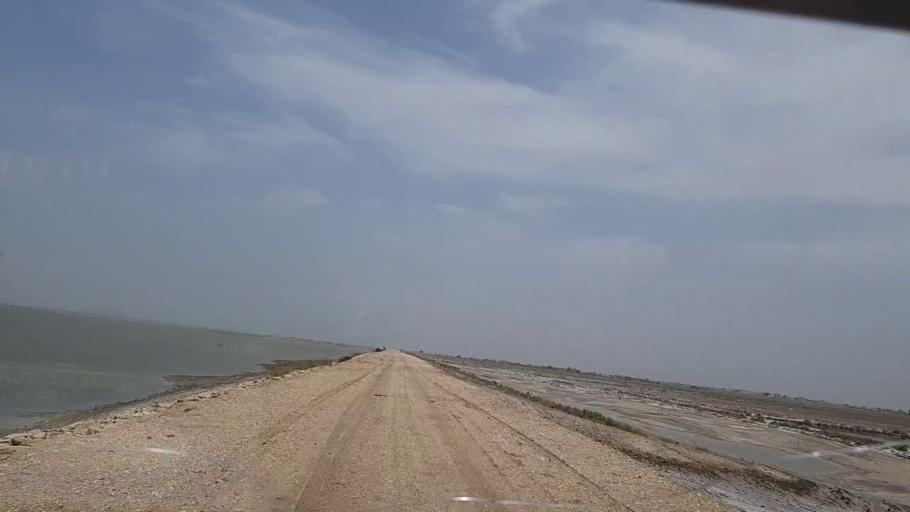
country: PK
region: Sindh
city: Sehwan
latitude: 26.4141
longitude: 67.7693
